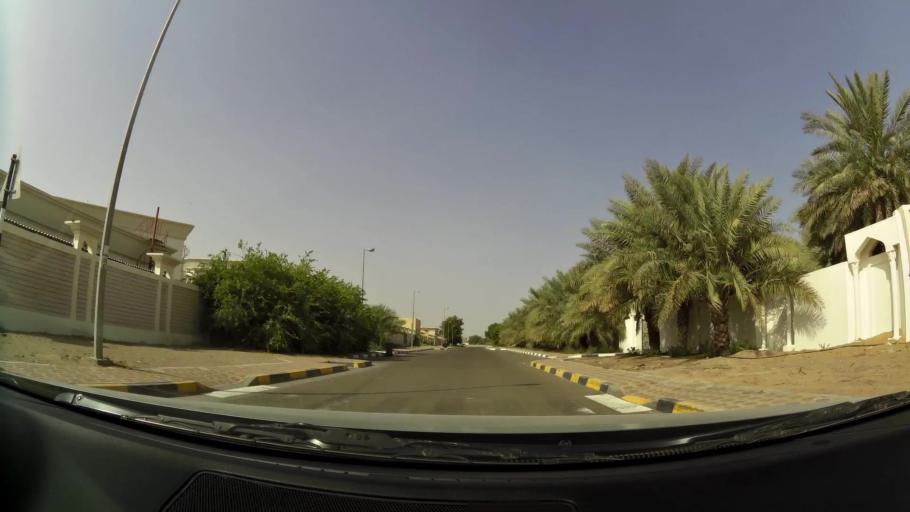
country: AE
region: Abu Dhabi
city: Al Ain
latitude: 24.2531
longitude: 55.6904
